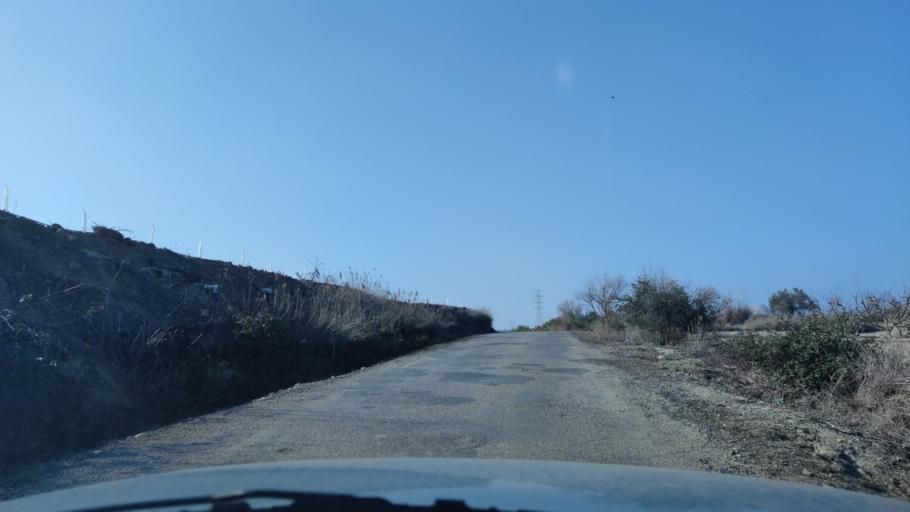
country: ES
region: Catalonia
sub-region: Provincia de Lleida
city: Seros
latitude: 41.4664
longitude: 0.3871
